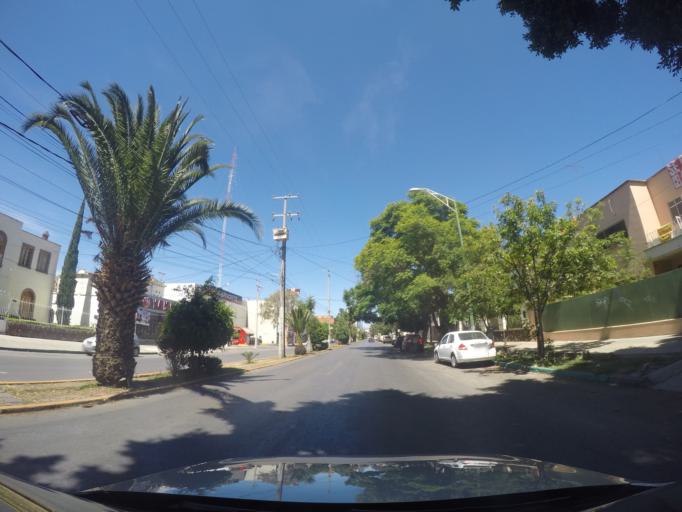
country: MX
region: San Luis Potosi
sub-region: San Luis Potosi
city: San Luis Potosi
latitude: 22.1499
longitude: -100.9956
